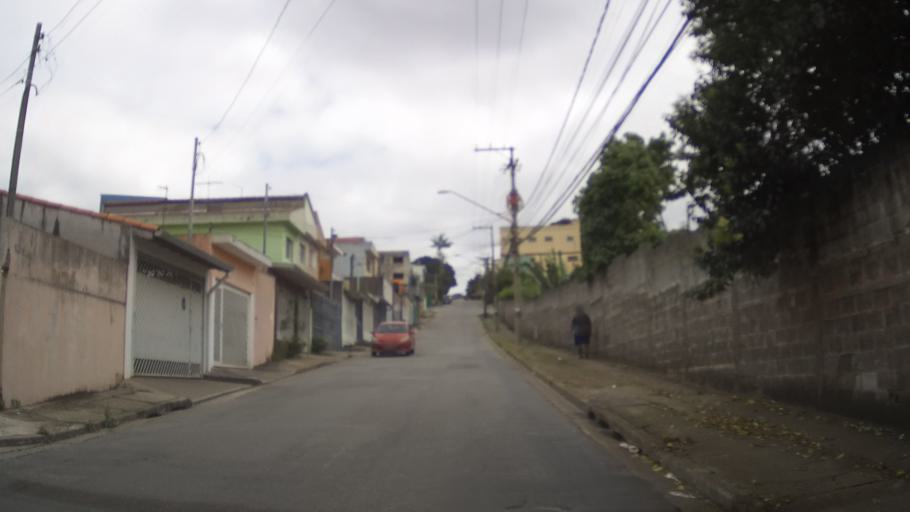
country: BR
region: Sao Paulo
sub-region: Guarulhos
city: Guarulhos
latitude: -23.4639
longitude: -46.5079
